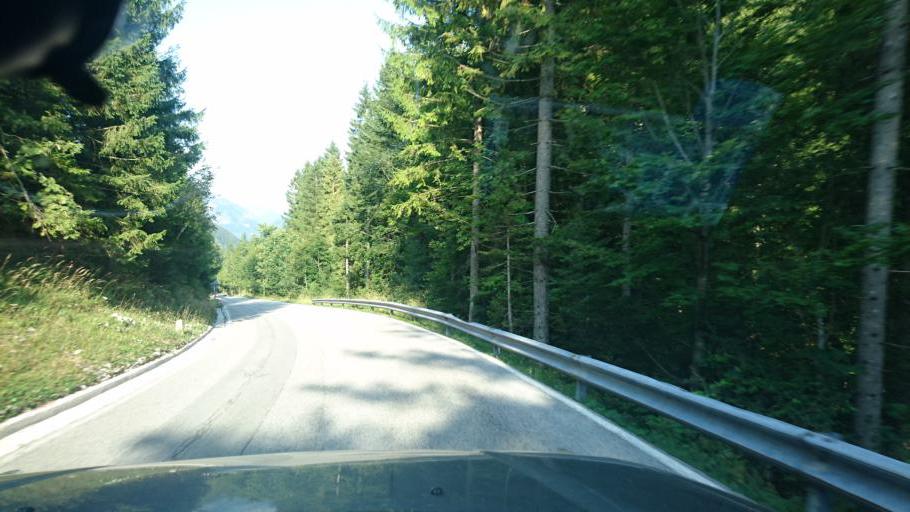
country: SI
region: Bovec
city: Bovec
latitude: 46.3954
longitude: 13.4979
